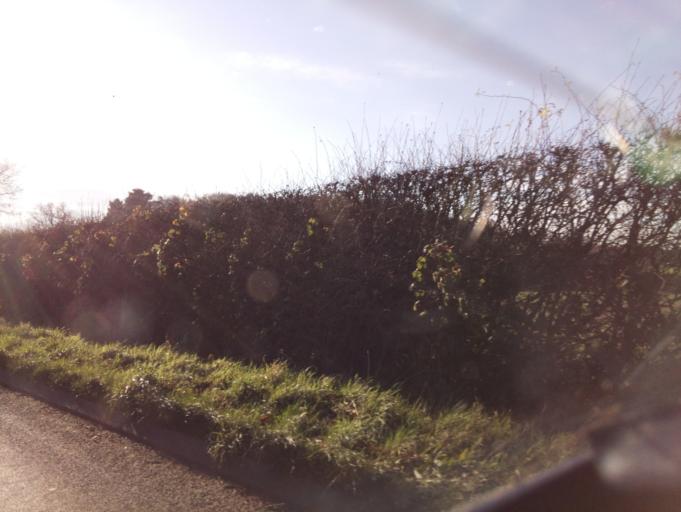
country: GB
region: England
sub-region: Staffordshire
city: Barton under Needwood
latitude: 52.8122
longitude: -1.7362
